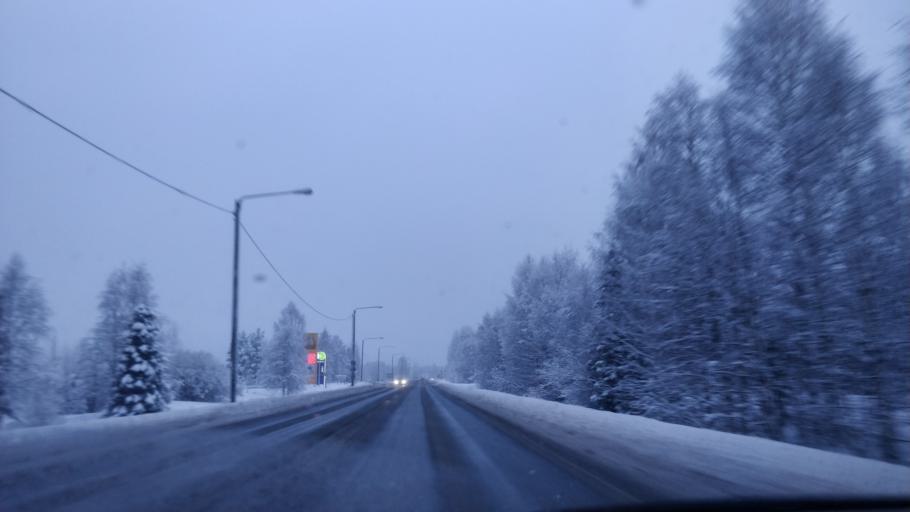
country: FI
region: Lapland
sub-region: Rovaniemi
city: Rovaniemi
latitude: 66.4767
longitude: 25.6229
